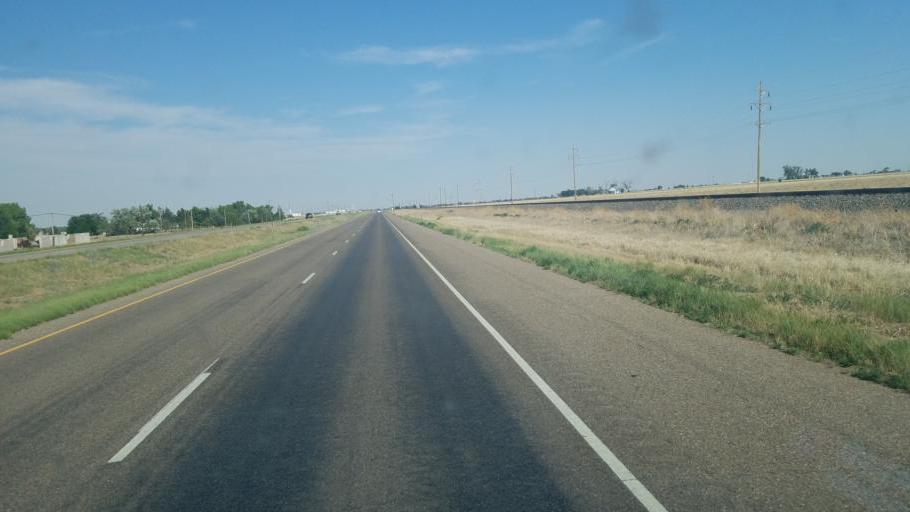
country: US
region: Colorado
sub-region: Otero County
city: Rocky Ford
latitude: 38.0371
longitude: -103.6804
